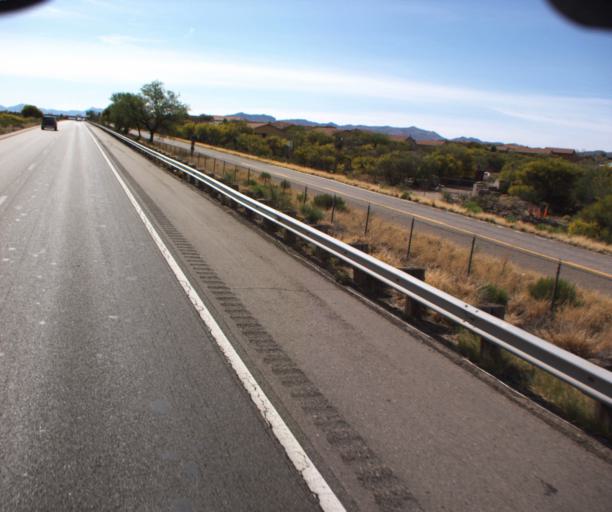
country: US
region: Arizona
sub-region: Pima County
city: Vail
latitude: 32.0120
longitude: -110.6980
